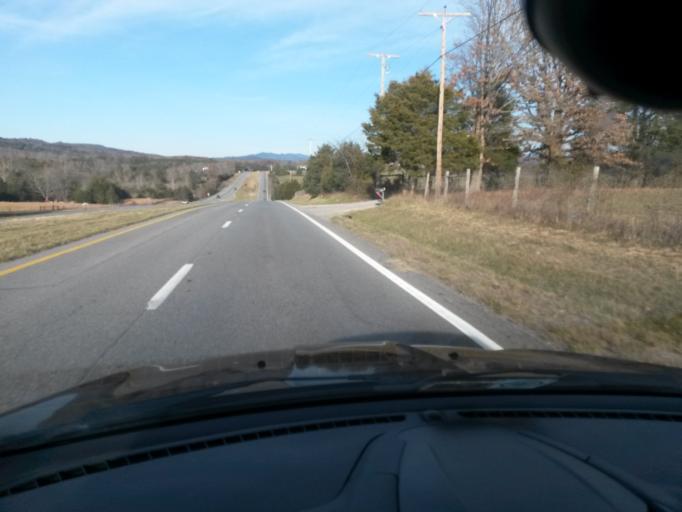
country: US
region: Virginia
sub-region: Botetourt County
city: Fincastle
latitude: 37.5406
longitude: -79.8632
